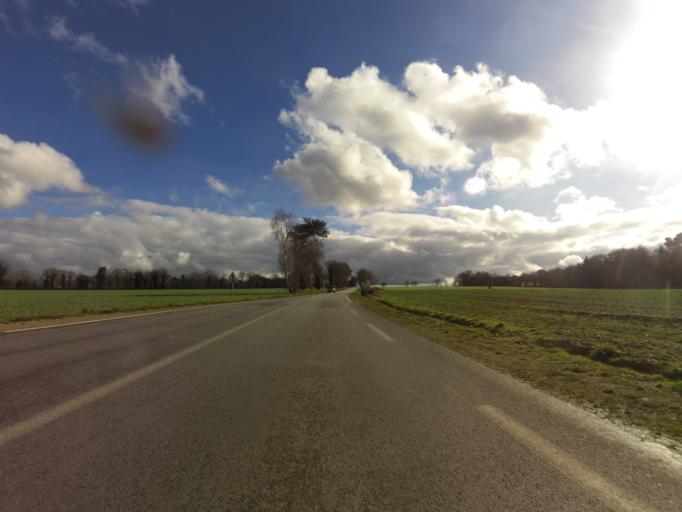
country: FR
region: Brittany
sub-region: Departement du Morbihan
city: Reguiny
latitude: 48.0015
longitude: -2.7470
